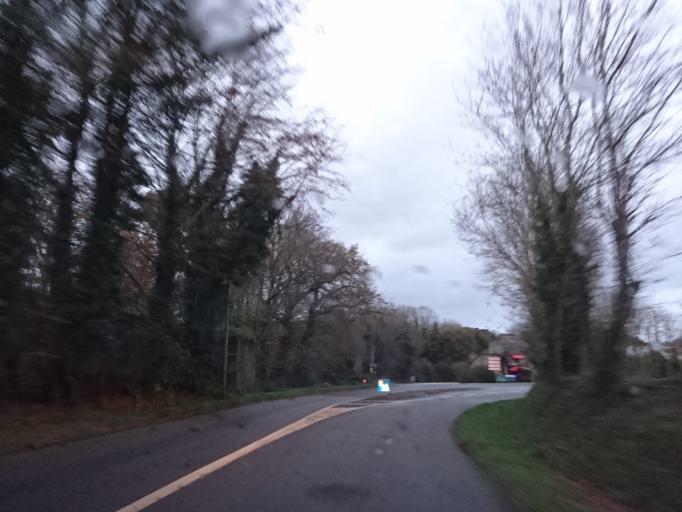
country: FR
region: Brittany
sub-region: Departement du Finistere
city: Le Conquet
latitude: 48.3632
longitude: -4.7477
